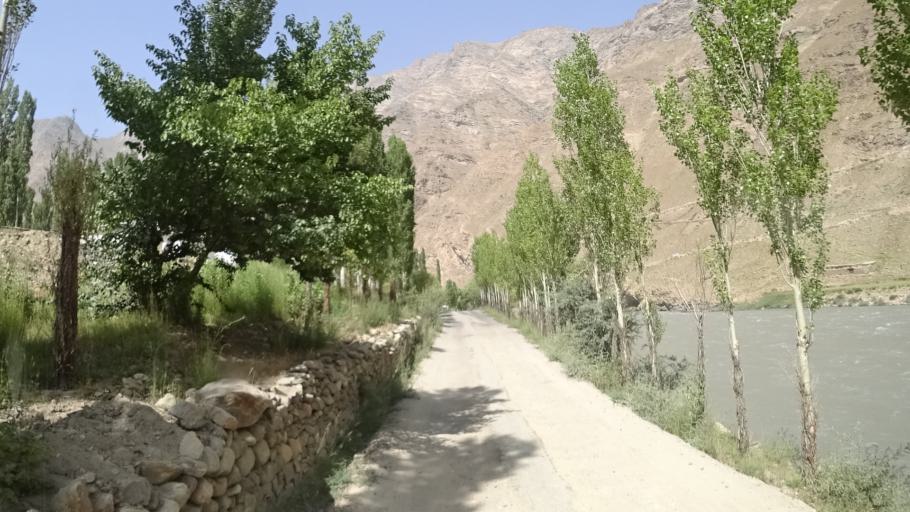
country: TJ
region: Gorno-Badakhshan
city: Khorugh
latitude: 37.1818
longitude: 71.4559
